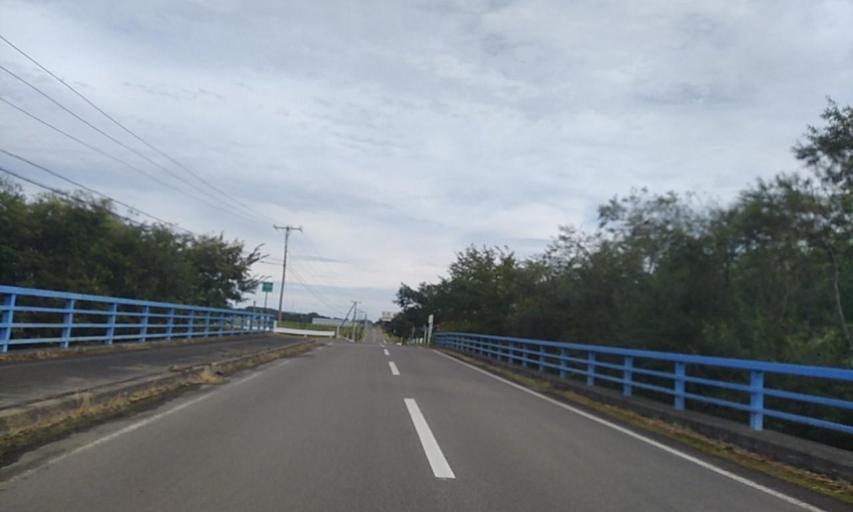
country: JP
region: Hokkaido
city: Abashiri
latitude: 43.7960
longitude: 144.5511
